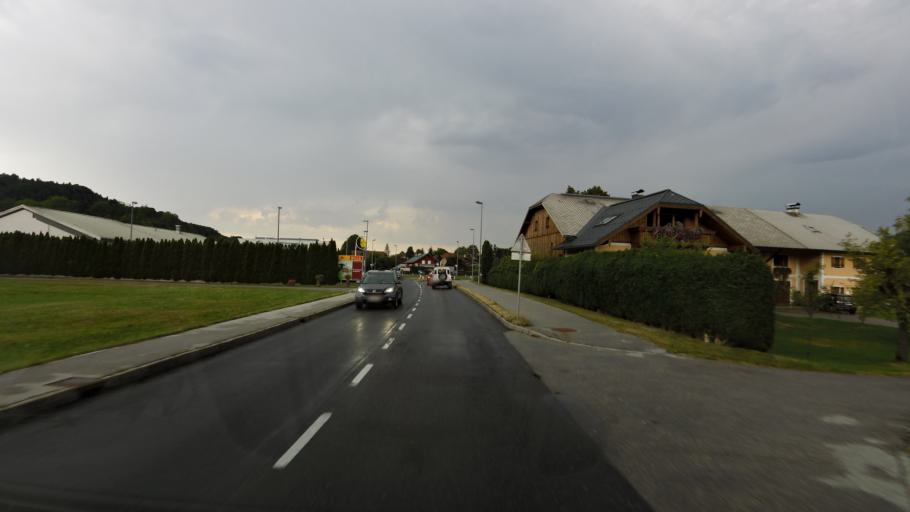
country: AT
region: Salzburg
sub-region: Politischer Bezirk Salzburg-Umgebung
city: Anif
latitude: 47.7210
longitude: 13.0613
